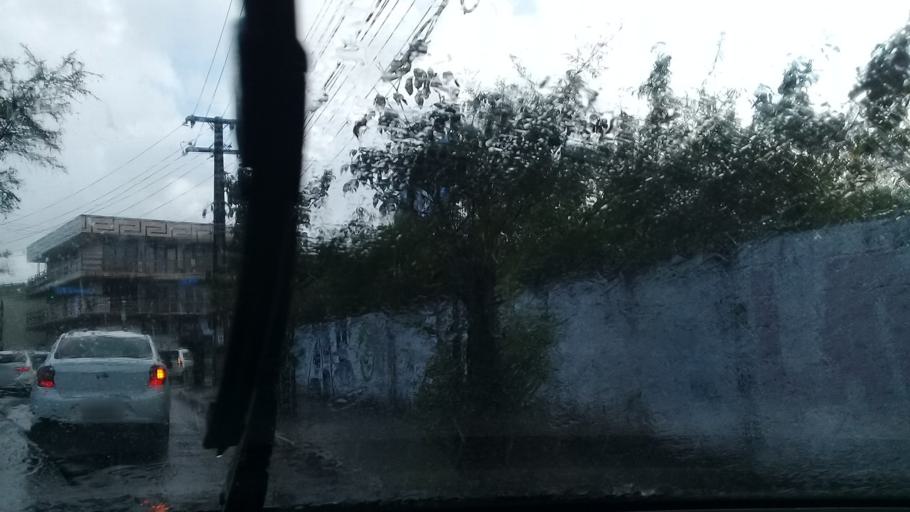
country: BR
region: Pernambuco
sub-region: Recife
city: Recife
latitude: -8.1324
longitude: -34.9111
